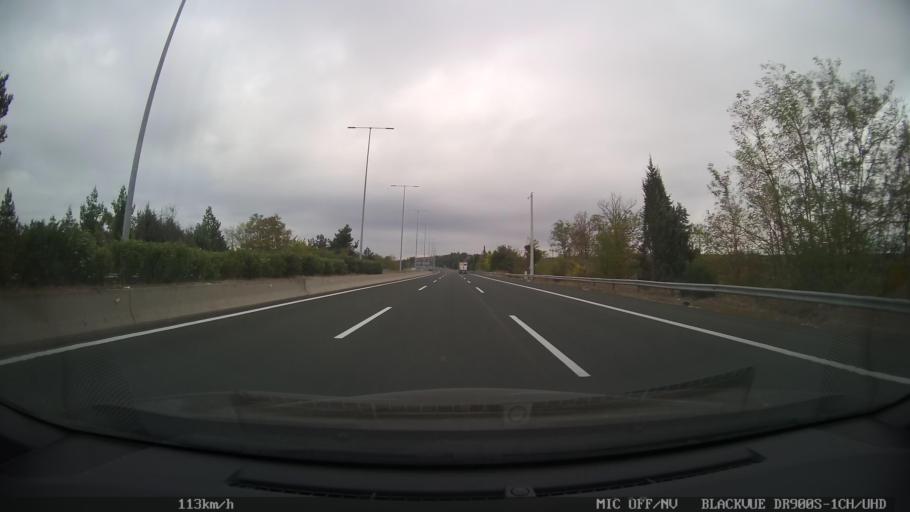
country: GR
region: Central Macedonia
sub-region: Nomos Pierias
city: Makrygialos
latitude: 40.4190
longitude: 22.5906
